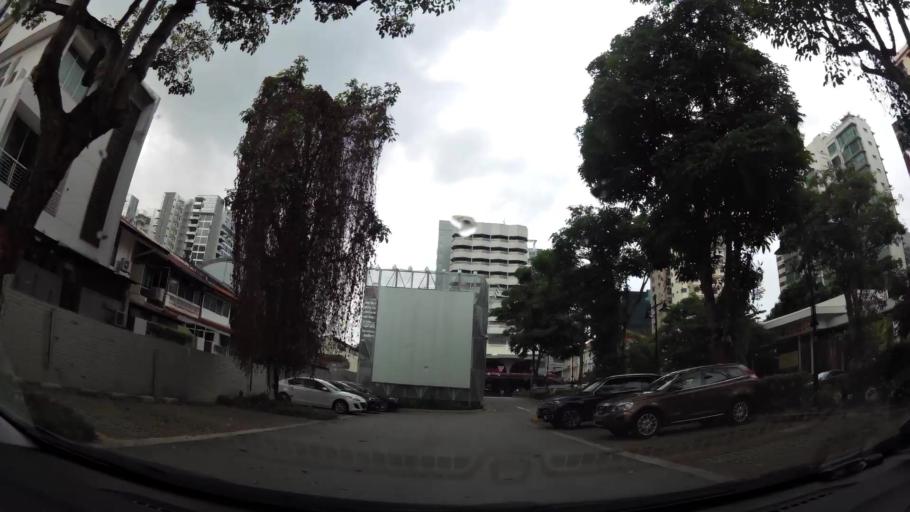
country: SG
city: Singapore
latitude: 1.3025
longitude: 103.9035
